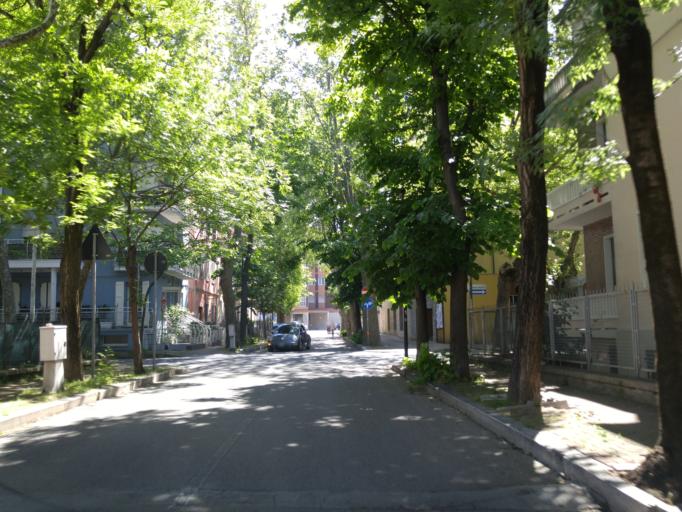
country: IT
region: The Marches
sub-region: Provincia di Pesaro e Urbino
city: Pesaro
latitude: 43.9090
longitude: 12.9222
